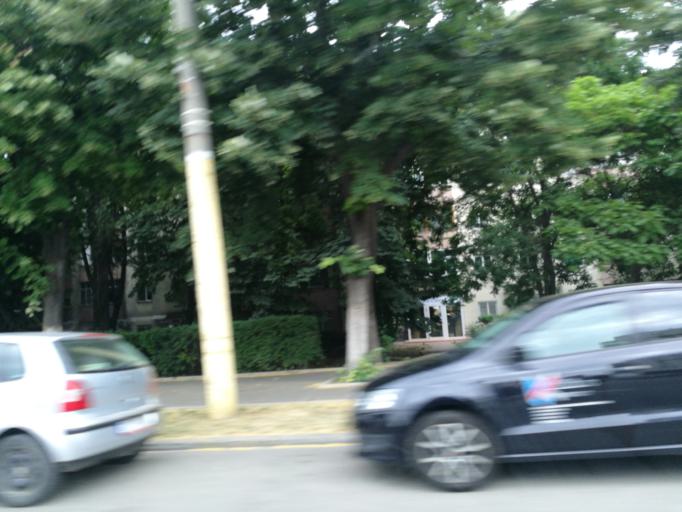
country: RO
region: Constanta
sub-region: Municipiul Constanta
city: Constanta
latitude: 44.1984
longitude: 28.6315
